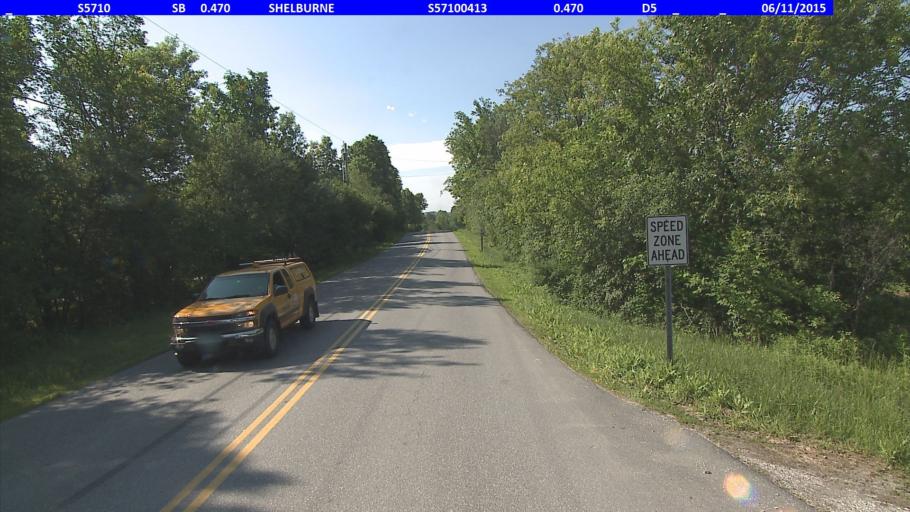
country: US
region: Vermont
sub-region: Chittenden County
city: Hinesburg
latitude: 44.3714
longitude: -73.1812
